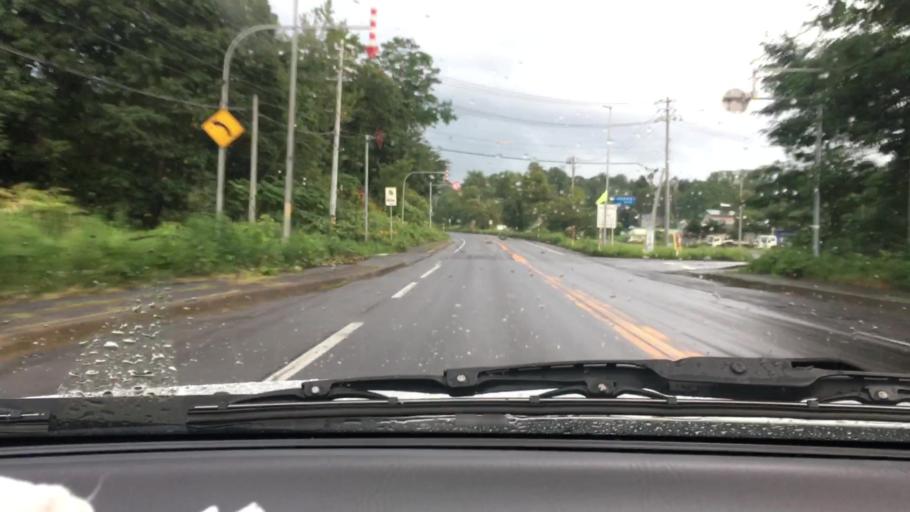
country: JP
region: Hokkaido
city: Nanae
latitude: 42.0842
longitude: 140.5856
